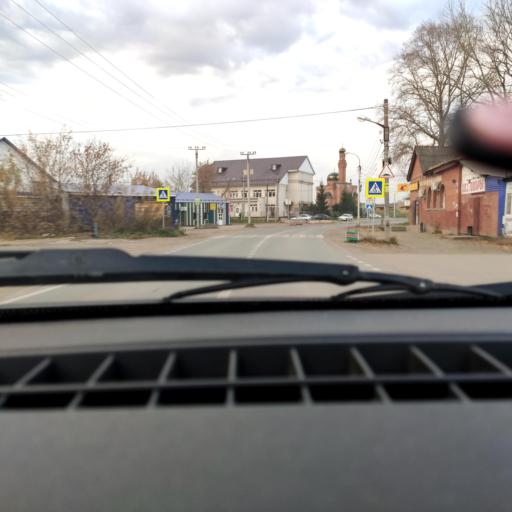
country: RU
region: Bashkortostan
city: Iglino
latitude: 54.8266
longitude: 56.1850
